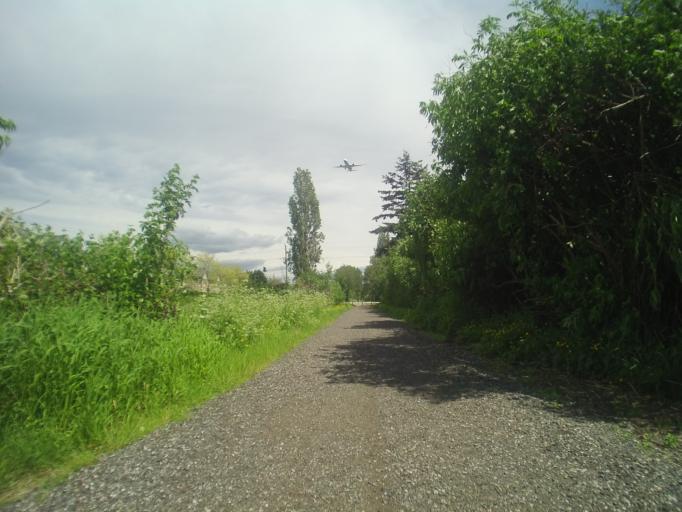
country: CA
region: British Columbia
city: Richmond
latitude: 49.1944
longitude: -123.1157
